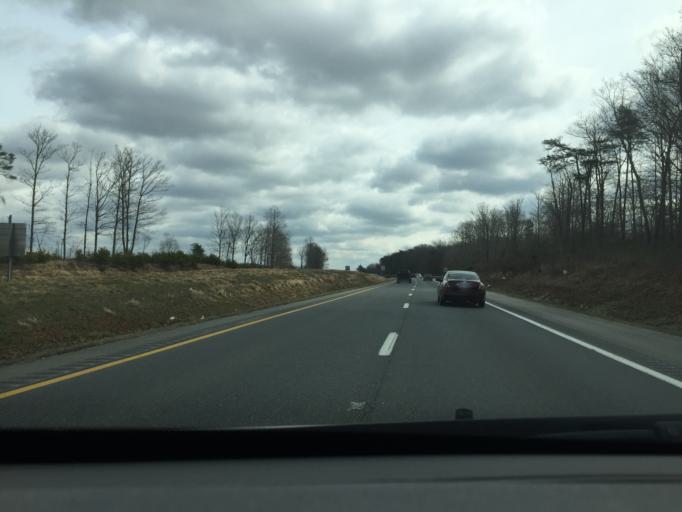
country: US
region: Virginia
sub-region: Campbell County
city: Timberlake
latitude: 37.3105
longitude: -79.2520
